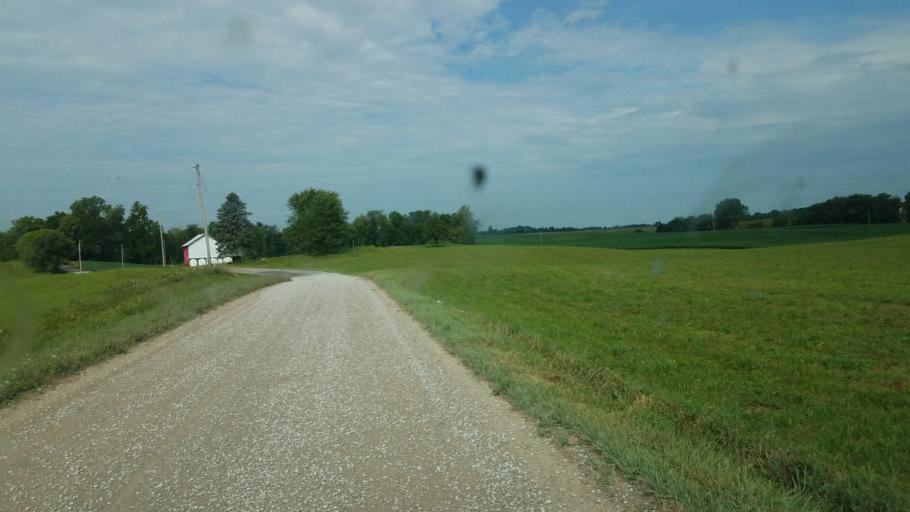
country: US
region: Ohio
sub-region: Knox County
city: Fredericktown
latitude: 40.4565
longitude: -82.6583
